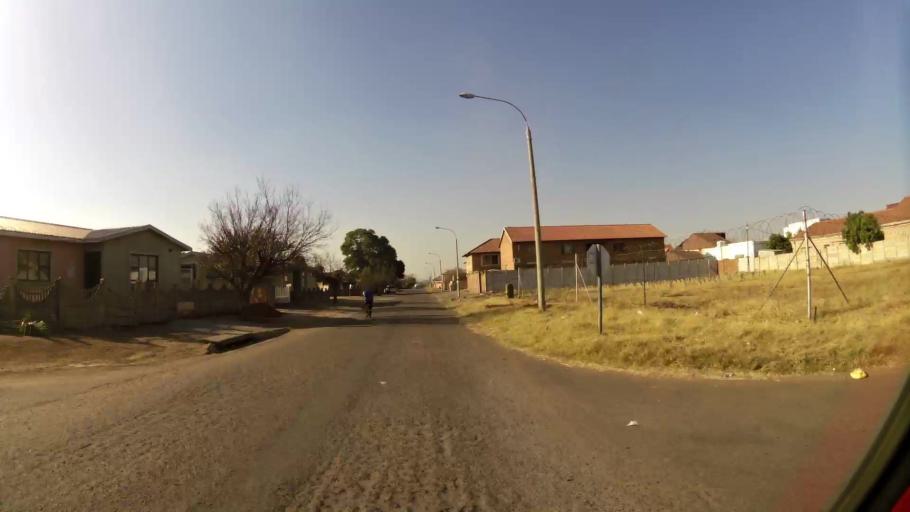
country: ZA
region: North-West
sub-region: Bojanala Platinum District Municipality
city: Rustenburg
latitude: -25.6443
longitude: 27.2390
